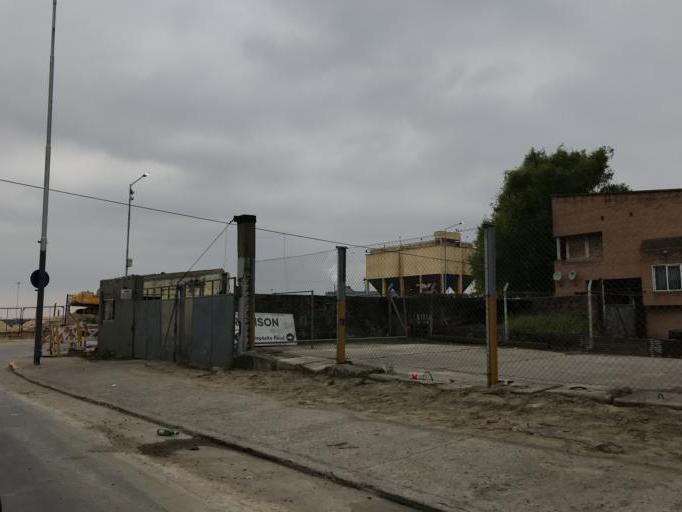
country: AR
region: Buenos Aires F.D.
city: Retiro
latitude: -34.5737
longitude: -58.3924
